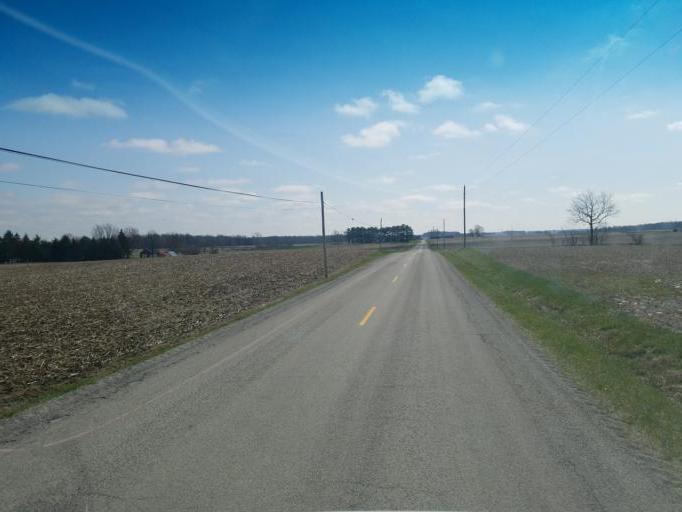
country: US
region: Ohio
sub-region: Crawford County
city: Bucyrus
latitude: 40.8999
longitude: -82.9270
